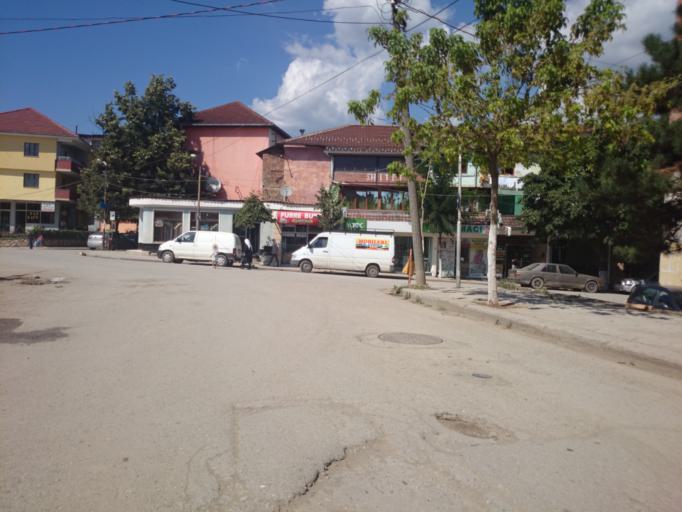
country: AL
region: Diber
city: Peshkopi
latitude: 41.6838
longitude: 20.4261
